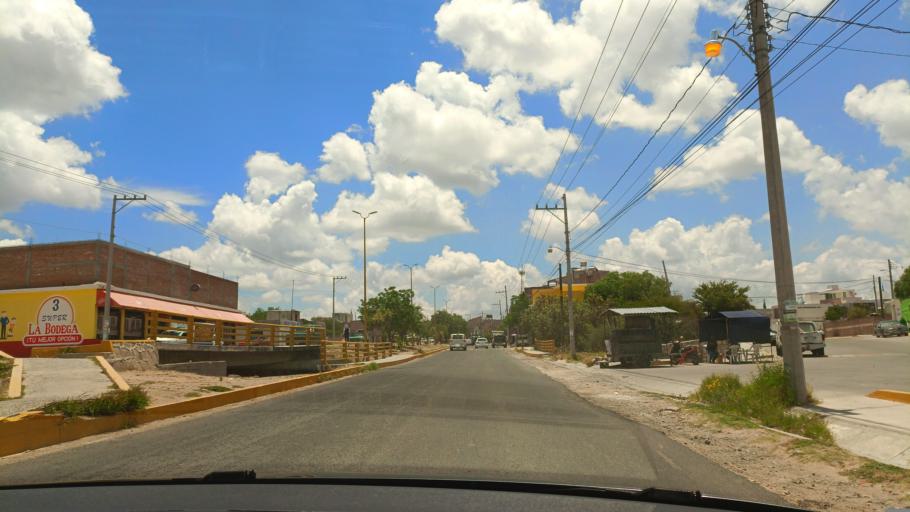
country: MX
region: Guanajuato
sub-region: San Luis de la Paz
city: San Ignacio
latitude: 21.2876
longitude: -100.5265
